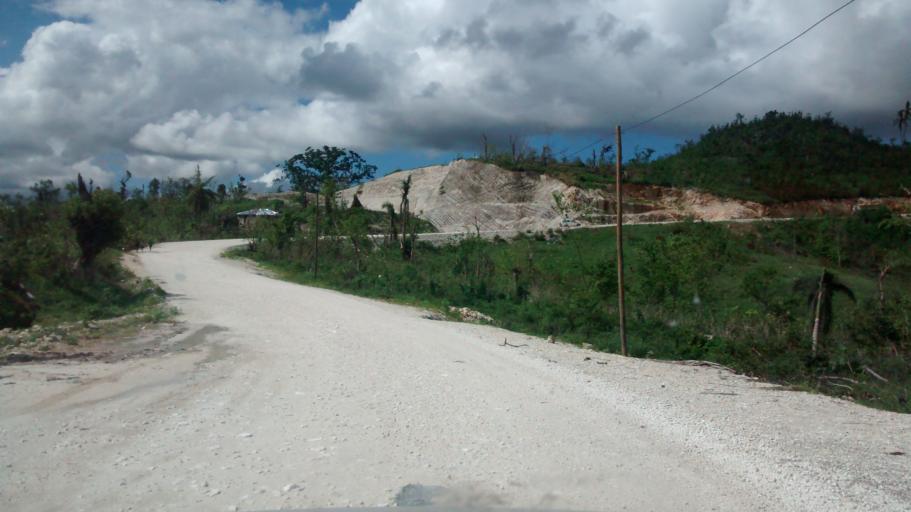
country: HT
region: Grandans
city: Corail
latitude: 18.5368
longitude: -73.9998
